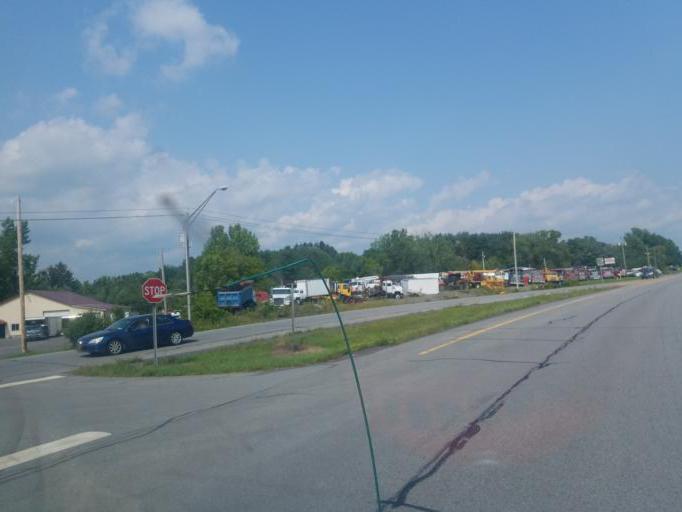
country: US
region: New York
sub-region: Fulton County
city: Johnstown
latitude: 42.9925
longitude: -74.3803
